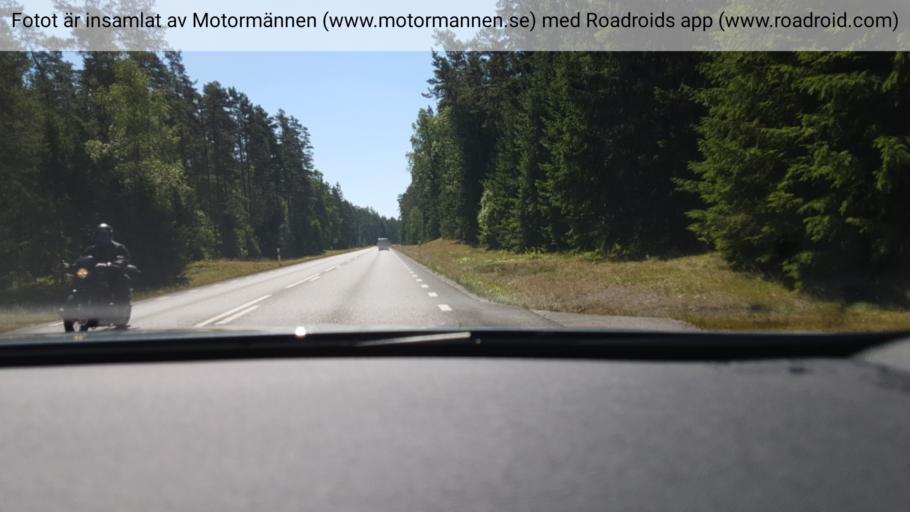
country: SE
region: Joenkoeping
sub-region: Gnosjo Kommun
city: Gnosjoe
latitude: 57.5062
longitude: 13.6777
